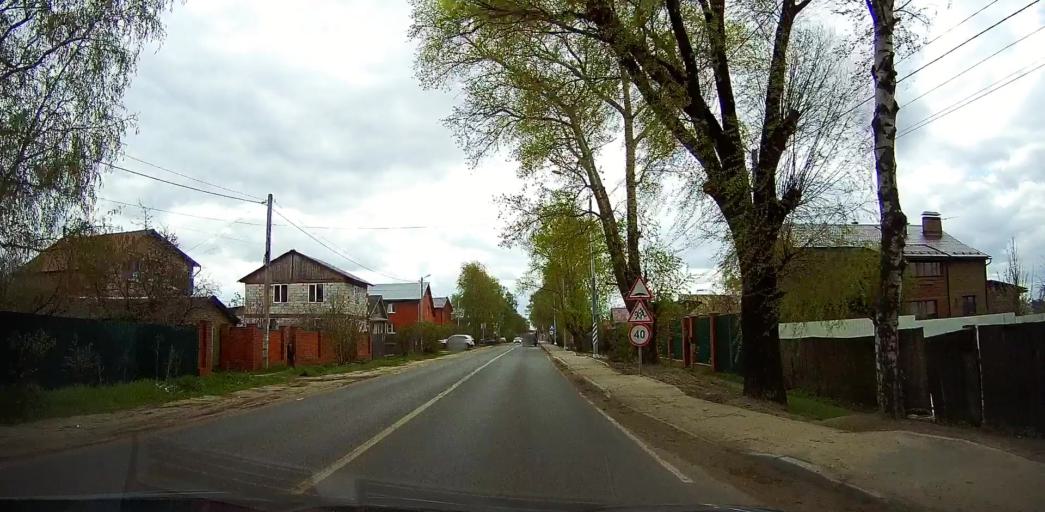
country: RU
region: Moskovskaya
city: Beloozerskiy
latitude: 55.4711
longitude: 38.4142
